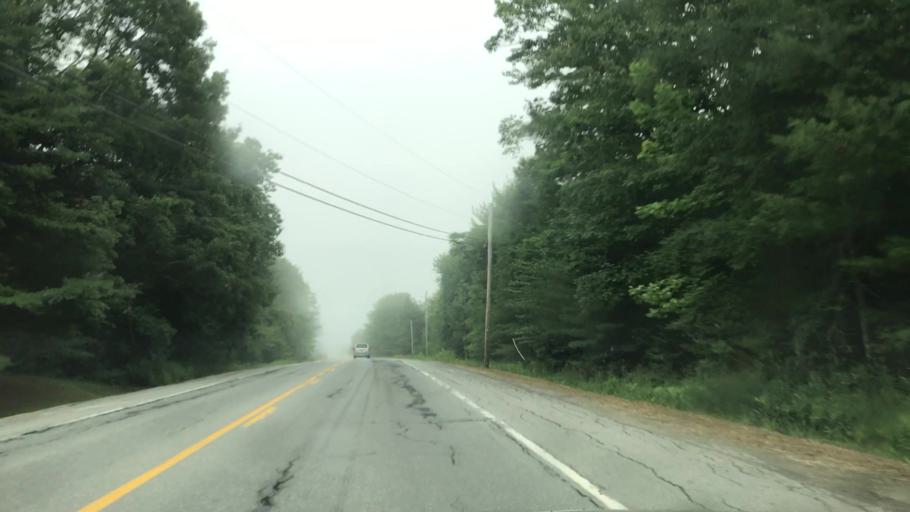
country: US
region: Maine
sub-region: Knox County
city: Warren
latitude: 44.1421
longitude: -69.2067
